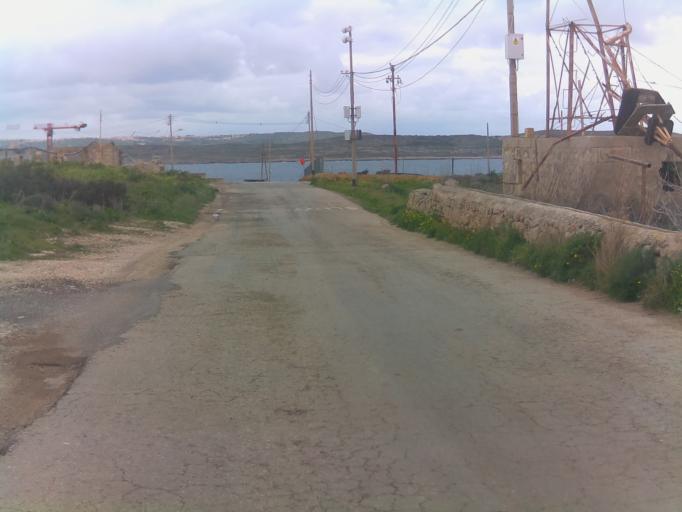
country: MT
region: Il-Mellieha
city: Mellieha
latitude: 35.9831
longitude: 14.3516
